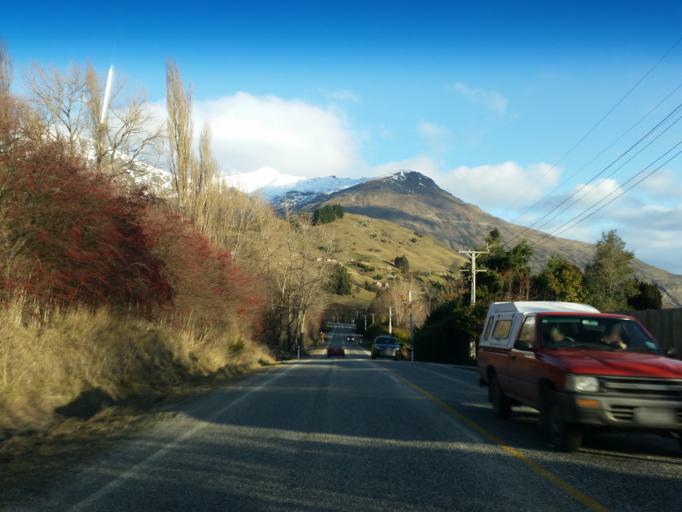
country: NZ
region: Otago
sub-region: Queenstown-Lakes District
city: Arrowtown
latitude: -44.9842
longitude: 168.8159
